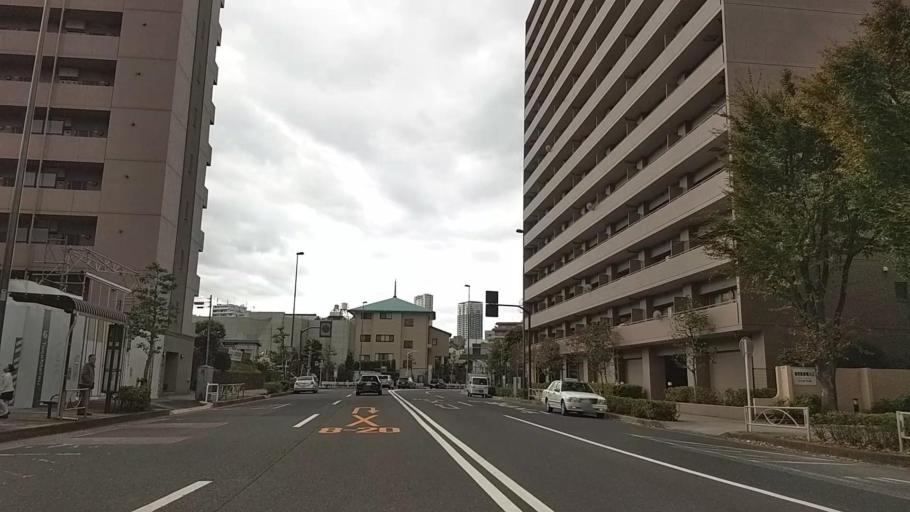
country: JP
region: Tokyo
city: Tokyo
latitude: 35.6464
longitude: 139.7399
